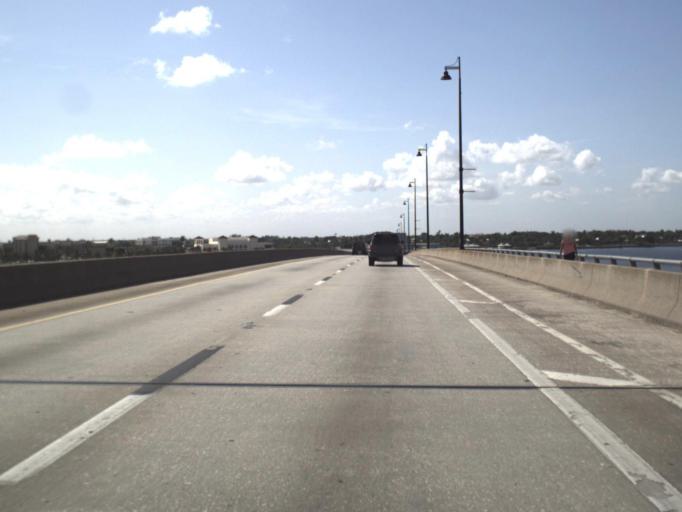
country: US
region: Florida
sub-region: Charlotte County
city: Charlotte Harbor
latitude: 26.9441
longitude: -82.0584
